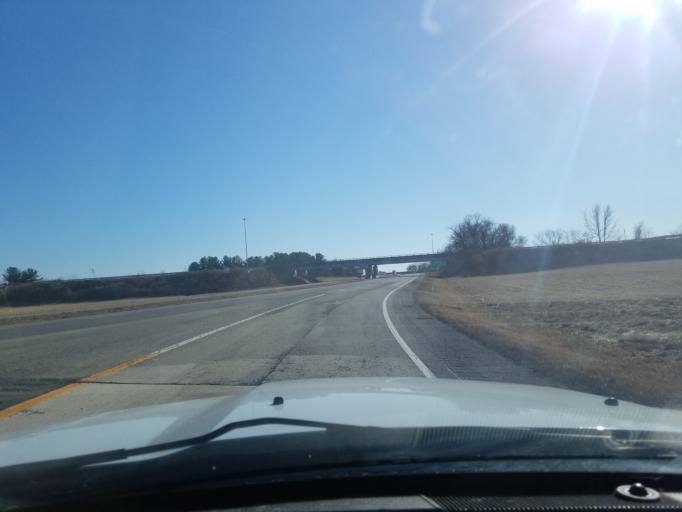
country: US
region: Kentucky
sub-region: Henderson County
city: Henderson
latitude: 37.8116
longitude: -87.5640
